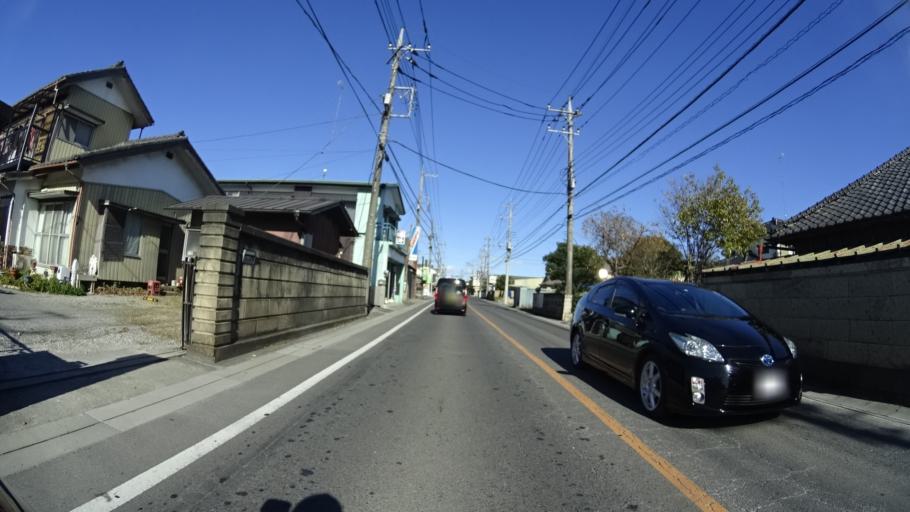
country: JP
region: Tochigi
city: Tochigi
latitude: 36.4042
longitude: 139.7419
